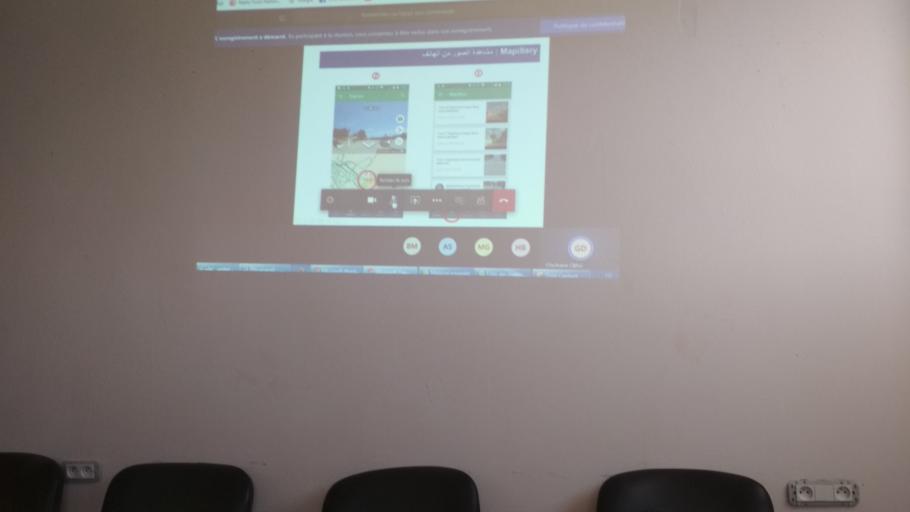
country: TN
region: Qabis
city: Gabes
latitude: 33.9398
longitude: 10.0644
